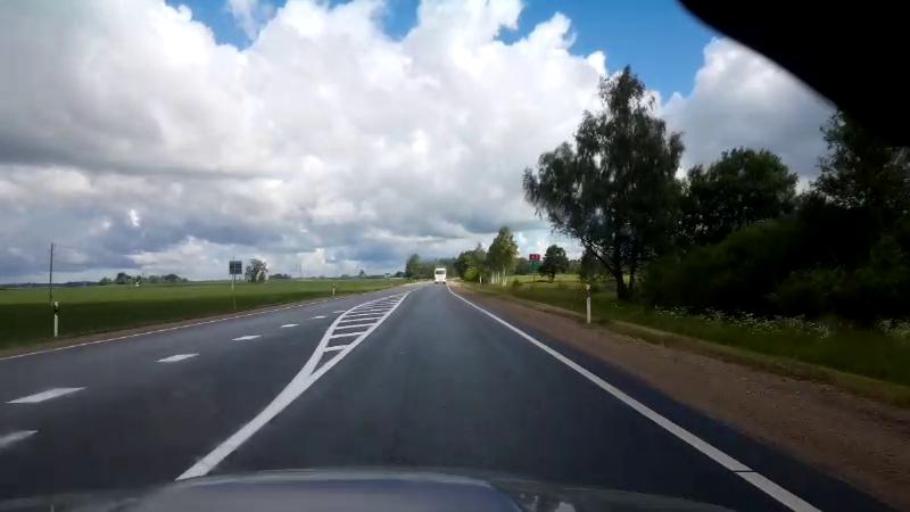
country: LV
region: Lecava
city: Iecava
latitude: 56.5075
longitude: 24.1731
